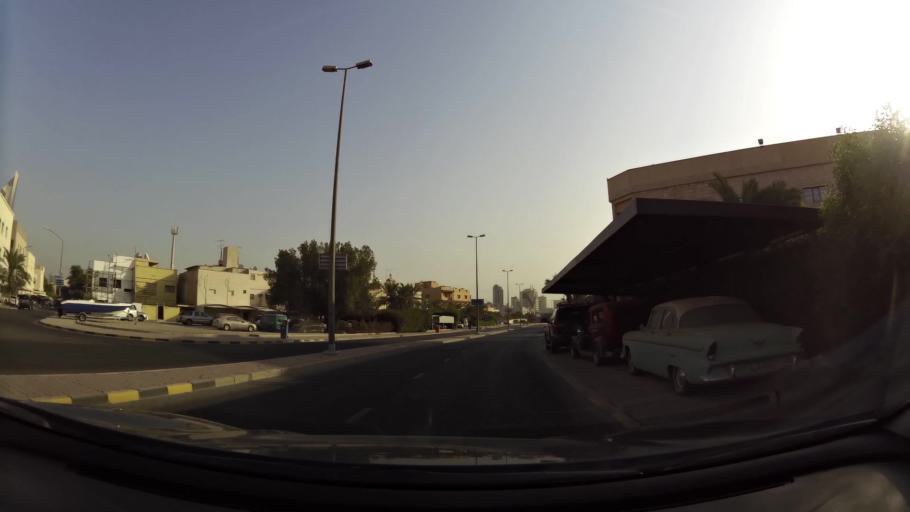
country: KW
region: Al Asimah
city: Ad Dasmah
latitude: 29.3646
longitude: 47.9965
